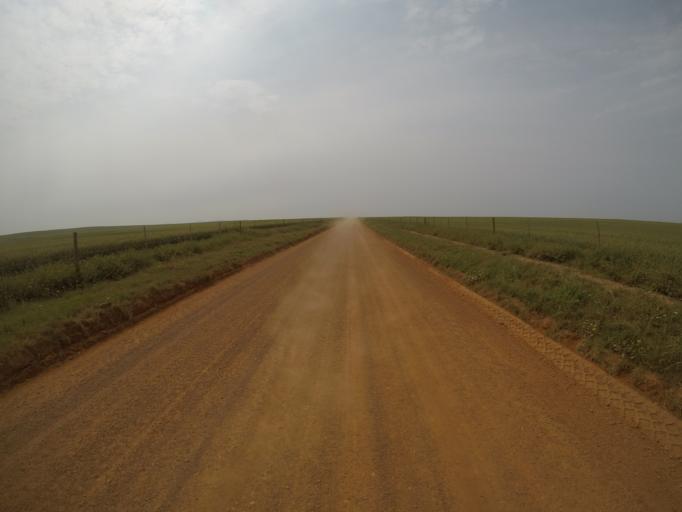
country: ZA
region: Western Cape
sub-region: City of Cape Town
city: Kraaifontein
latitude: -33.7231
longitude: 18.6707
